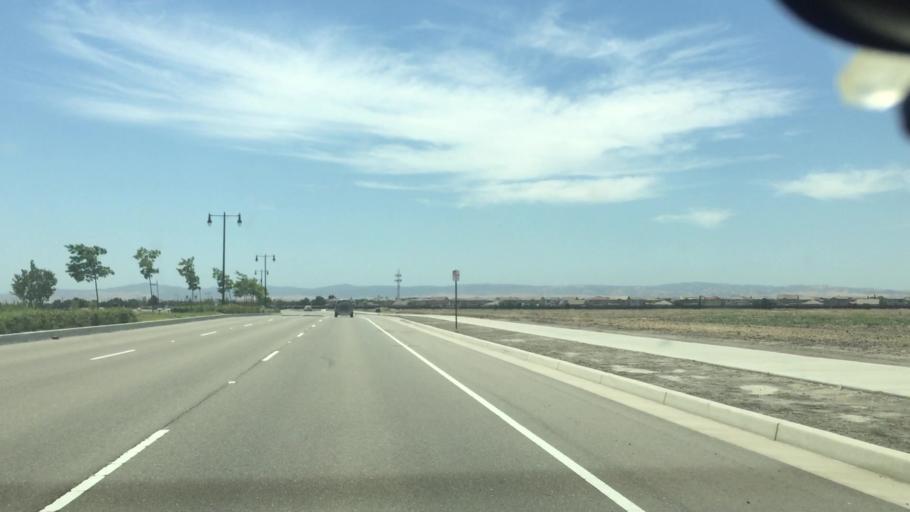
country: US
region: California
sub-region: San Joaquin County
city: Lathrop
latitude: 37.8185
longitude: -121.2987
